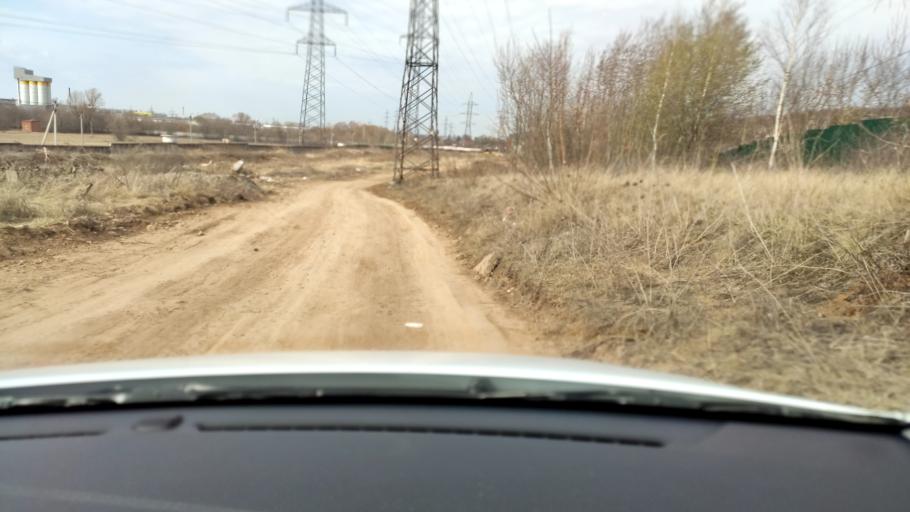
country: RU
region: Tatarstan
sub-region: Gorod Kazan'
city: Kazan
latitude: 55.8171
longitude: 49.2116
